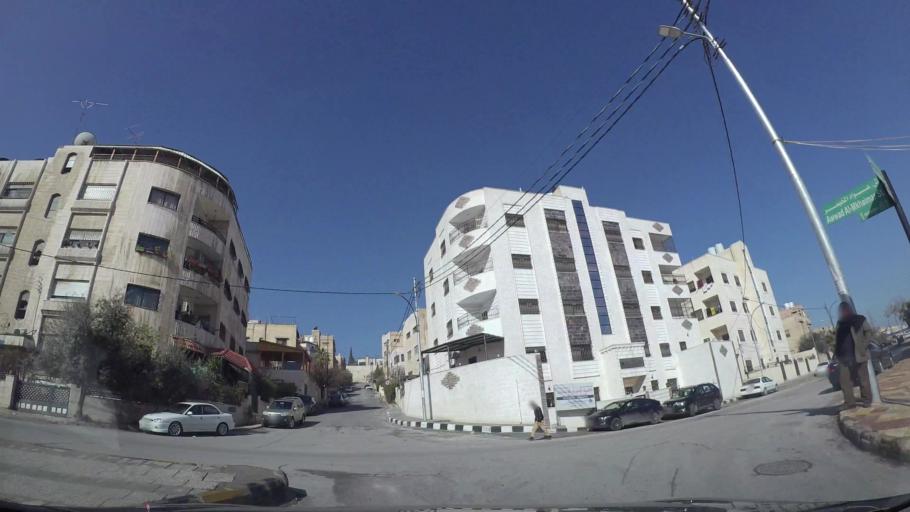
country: JO
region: Amman
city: Amman
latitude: 31.9857
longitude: 35.9925
